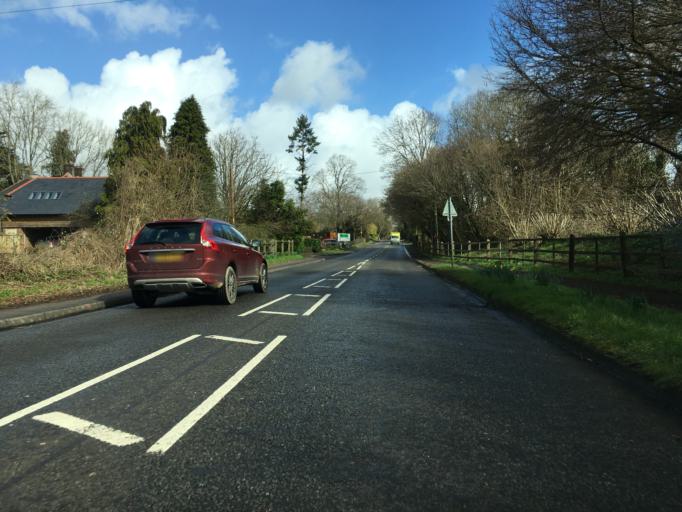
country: GB
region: England
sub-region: Hampshire
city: Compton
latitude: 51.0132
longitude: -1.3403
